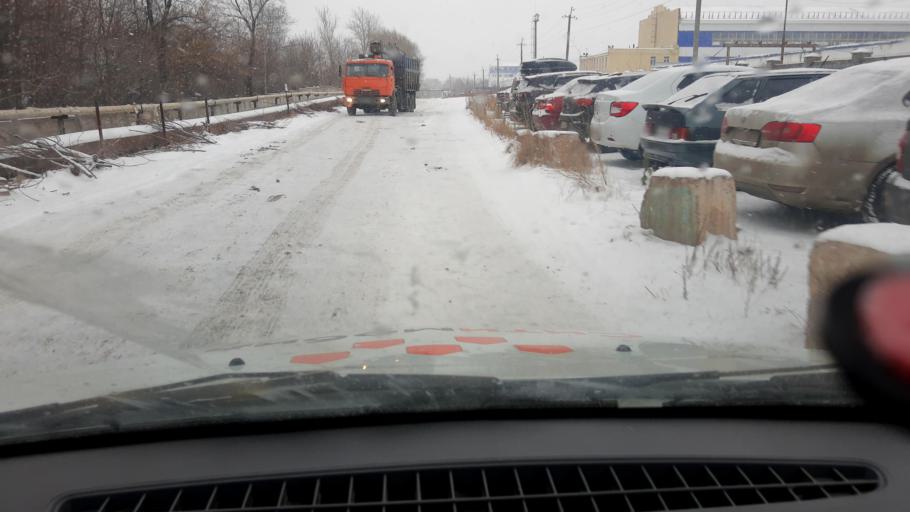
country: RU
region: Bashkortostan
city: Blagoveshchensk
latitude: 54.9124
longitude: 56.0776
